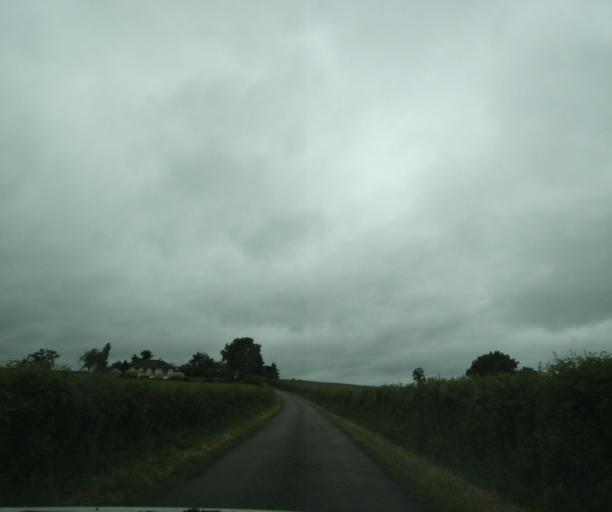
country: FR
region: Bourgogne
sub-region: Departement de Saone-et-Loire
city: Genelard
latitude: 46.5751
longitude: 4.2165
